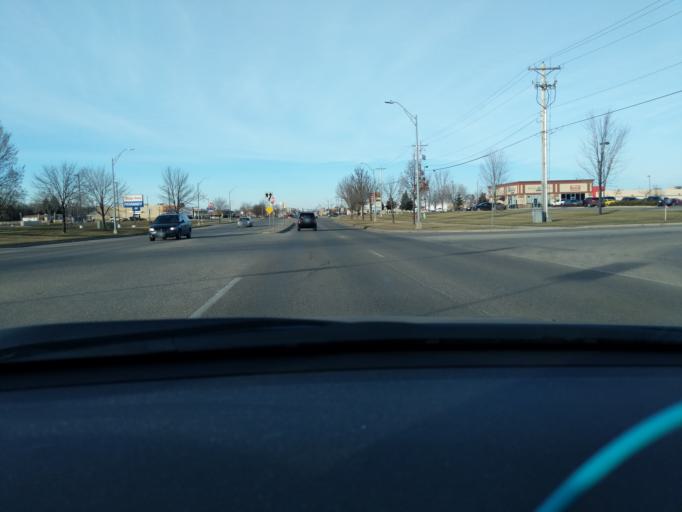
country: US
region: Minnesota
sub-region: Kandiyohi County
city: Willmar
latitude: 45.0991
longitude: -95.0426
